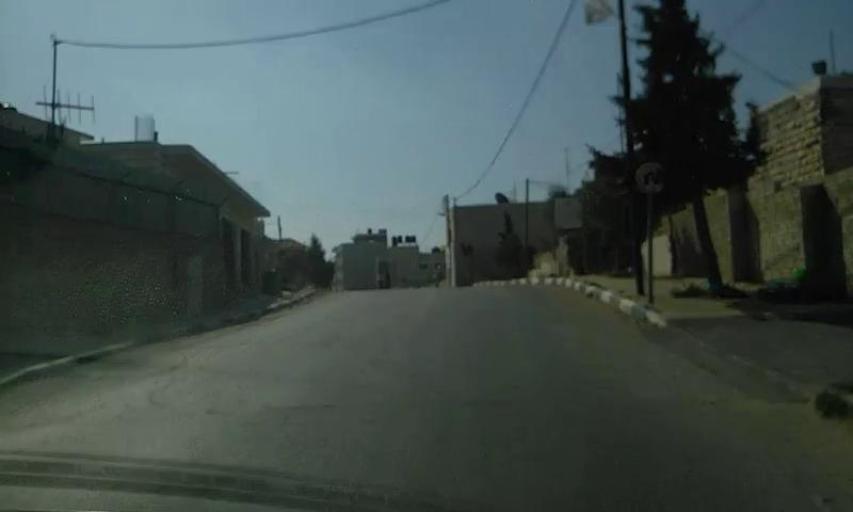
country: PS
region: West Bank
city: At Taybah
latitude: 31.9582
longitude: 35.2974
